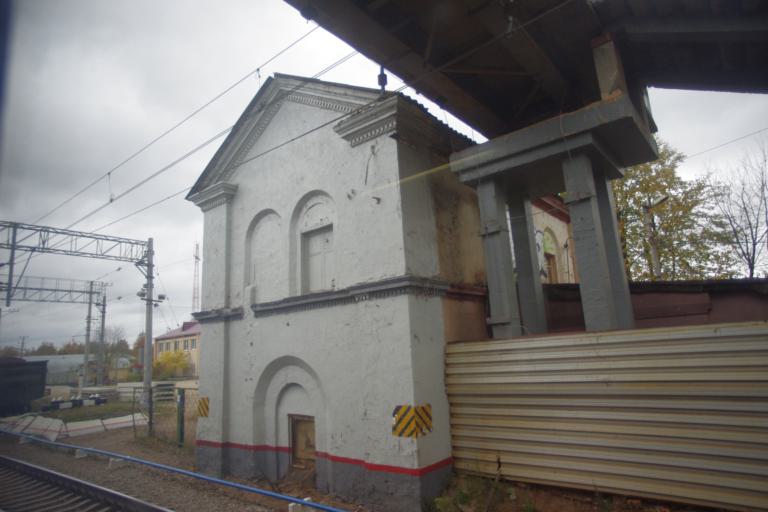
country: RU
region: Moskovskaya
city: Solnechnogorsk
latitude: 56.1846
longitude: 36.9704
